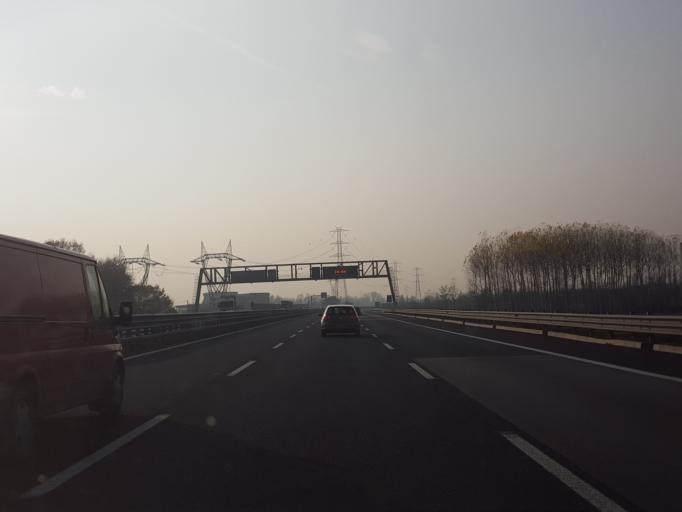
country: IT
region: Veneto
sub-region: Provincia di Treviso
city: Preganziol
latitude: 45.5902
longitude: 12.2500
